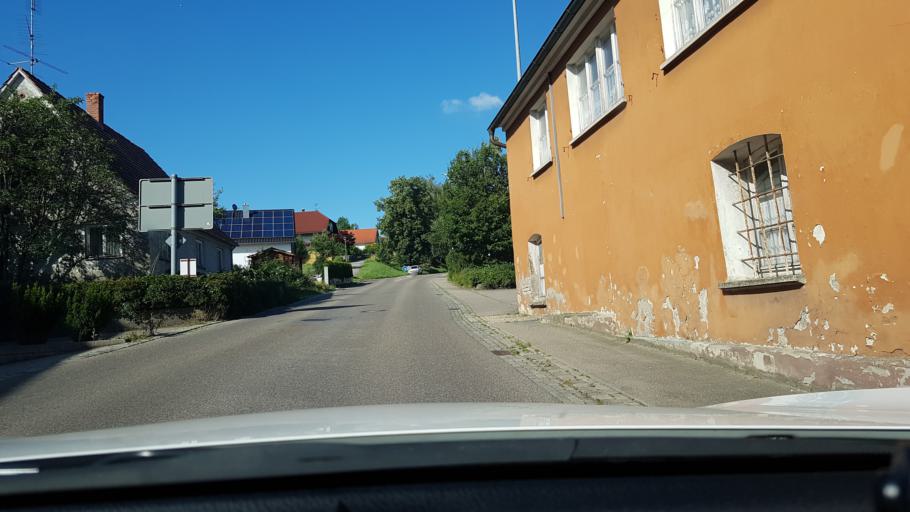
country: DE
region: Baden-Wuerttemberg
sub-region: Tuebingen Region
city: Schwendi
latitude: 48.1564
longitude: 9.9469
